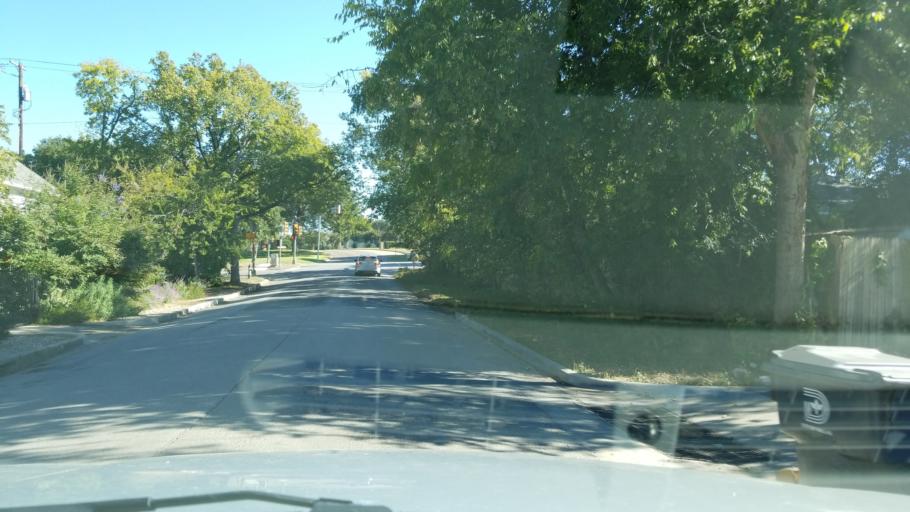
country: US
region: Texas
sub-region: Dallas County
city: Highland Park
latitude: 32.7997
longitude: -96.7418
